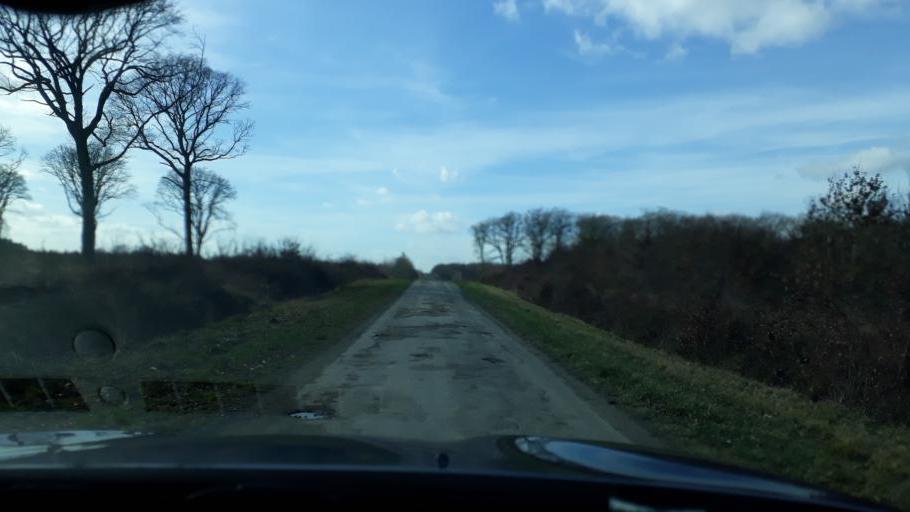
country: FR
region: Centre
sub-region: Departement du Loiret
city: Trainou
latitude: 47.9959
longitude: 2.1359
